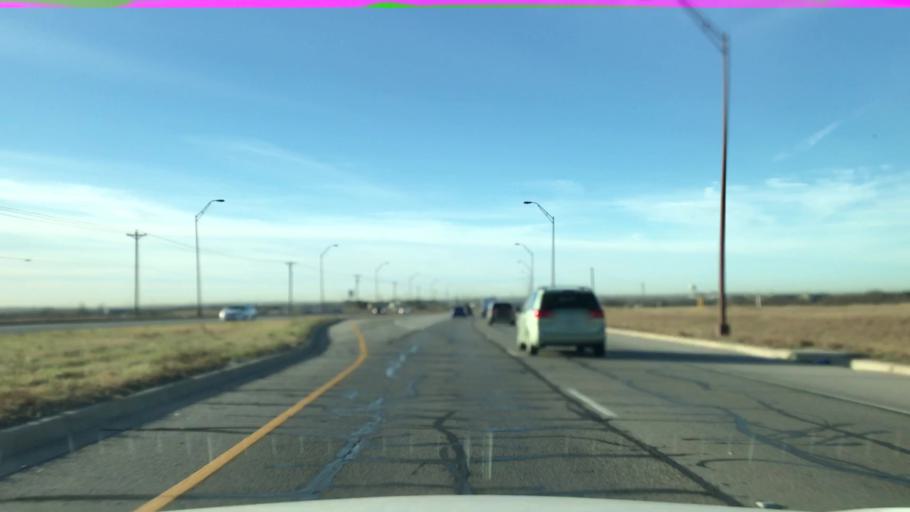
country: US
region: Texas
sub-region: Williamson County
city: Round Rock
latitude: 30.5556
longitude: -97.6459
